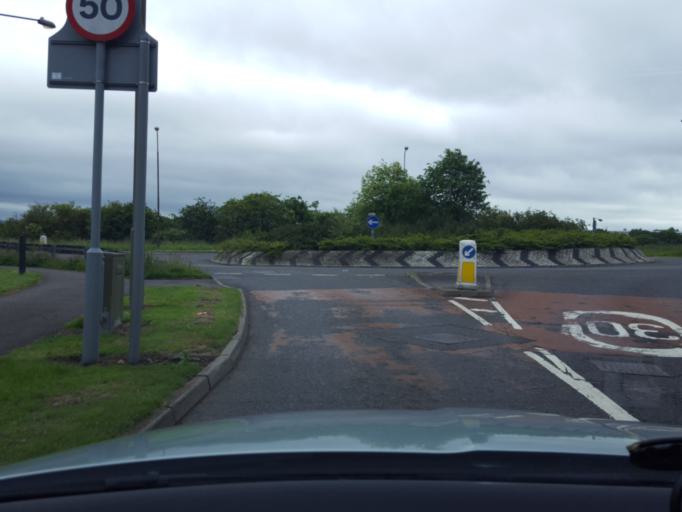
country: GB
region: Scotland
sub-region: West Lothian
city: Broxburn
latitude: 55.9276
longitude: -3.4945
